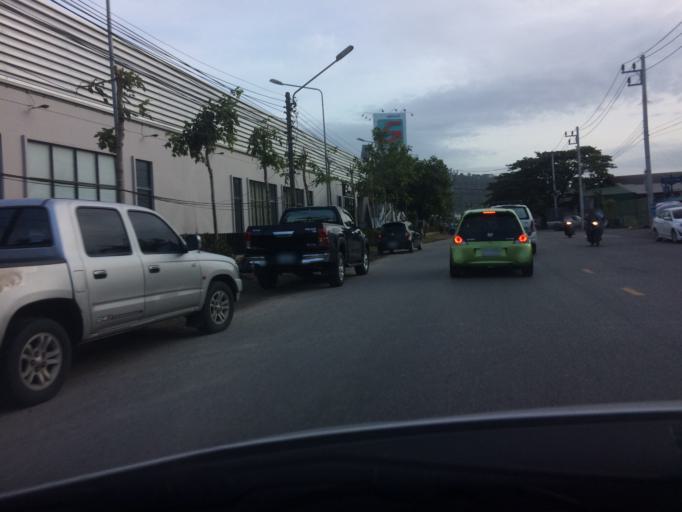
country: TH
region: Phuket
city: Ban Talat Yai
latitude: 7.8774
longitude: 98.3986
